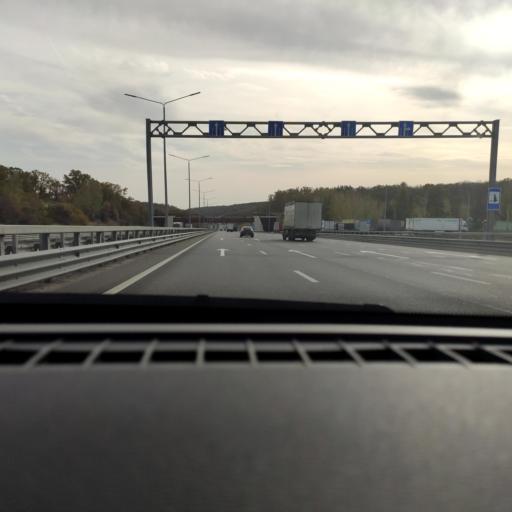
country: RU
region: Voronezj
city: Podgornoye
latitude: 51.8113
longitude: 39.2522
